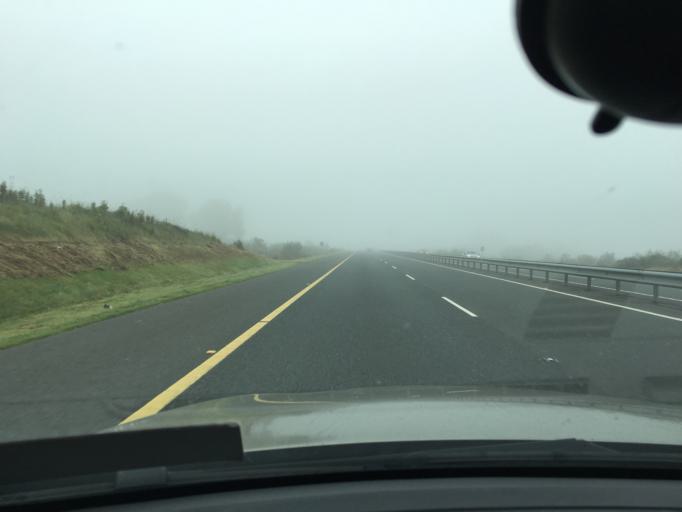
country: IE
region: Leinster
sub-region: An Iarmhi
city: Athlone
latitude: 53.4059
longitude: -8.0274
